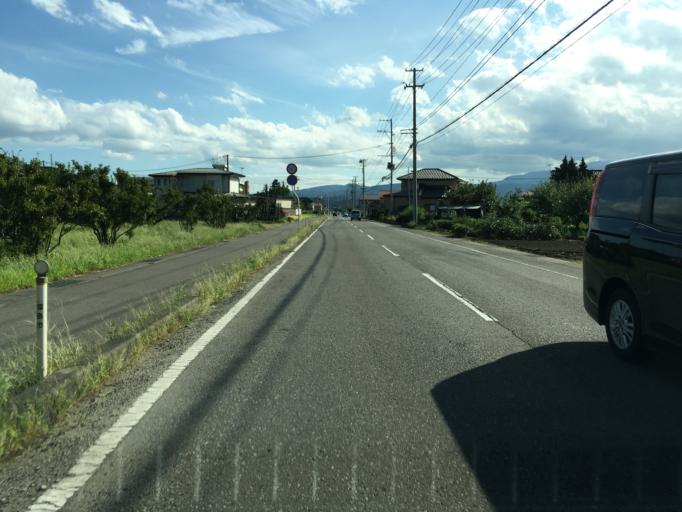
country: JP
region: Fukushima
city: Fukushima-shi
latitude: 37.7636
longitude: 140.4215
